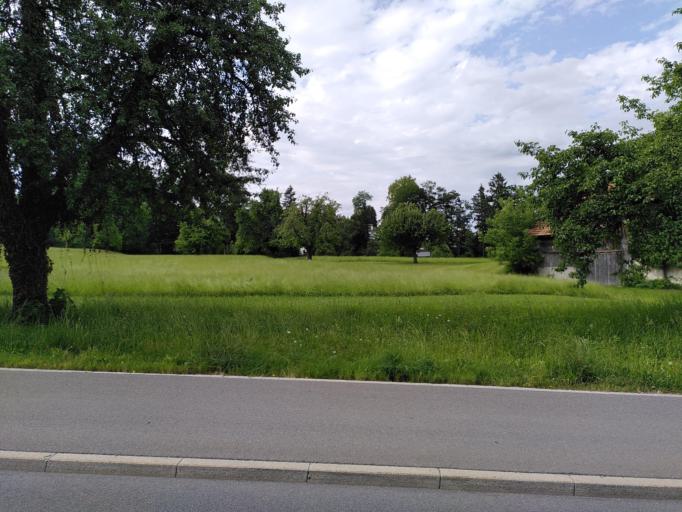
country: CH
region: Zurich
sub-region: Bezirk Horgen
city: Richterswil
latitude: 47.2063
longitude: 8.6970
